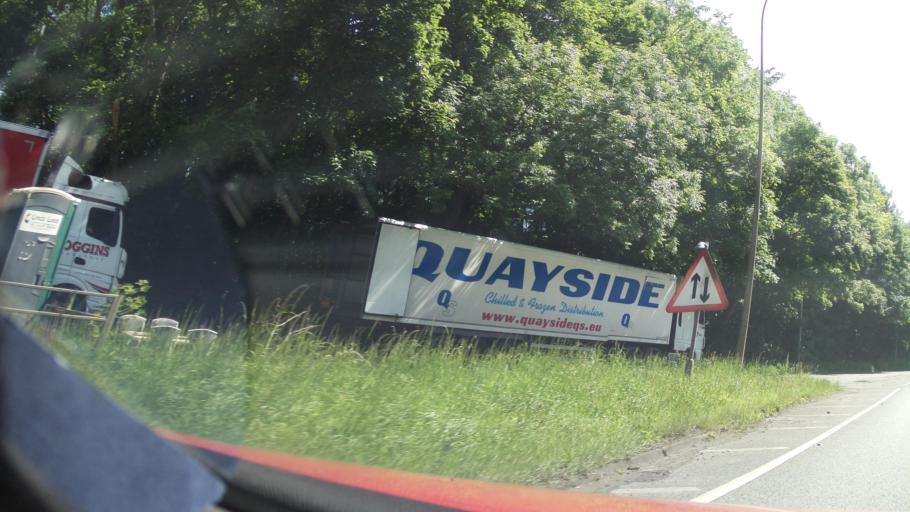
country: GB
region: England
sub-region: North Lincolnshire
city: Broughton
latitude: 53.5524
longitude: -0.5738
